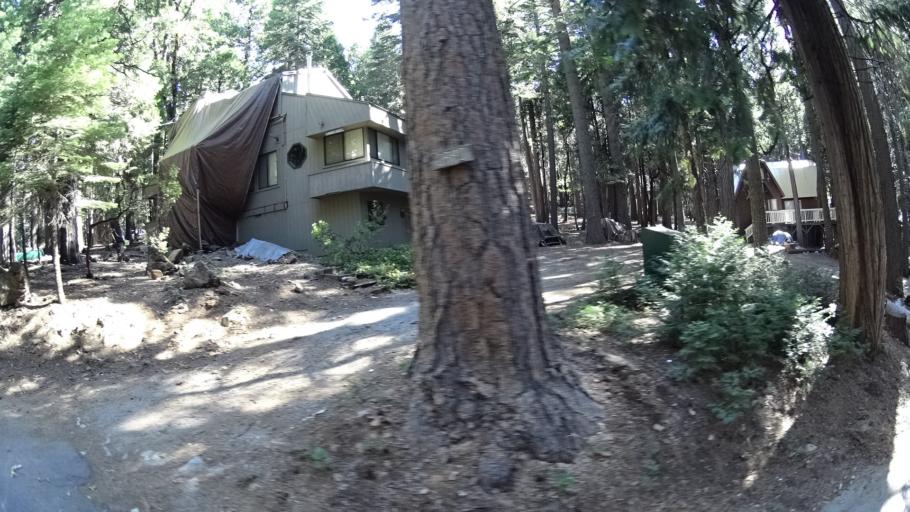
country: US
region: California
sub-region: Calaveras County
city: Arnold
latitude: 38.3031
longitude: -120.2715
